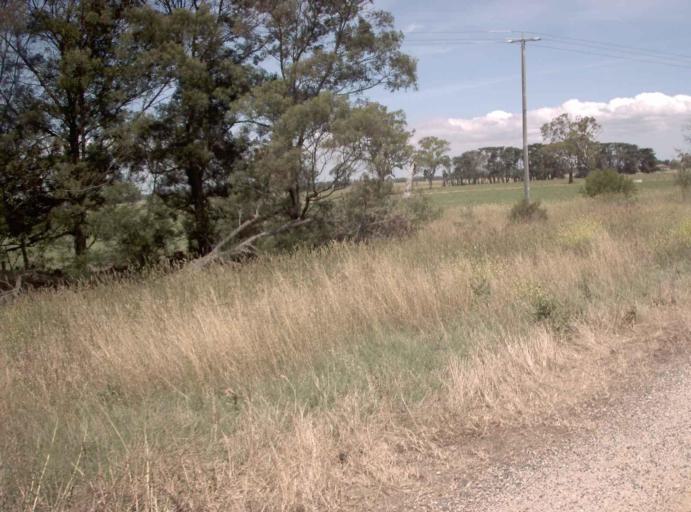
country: AU
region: Victoria
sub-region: Wellington
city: Heyfield
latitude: -38.0131
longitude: 146.8826
